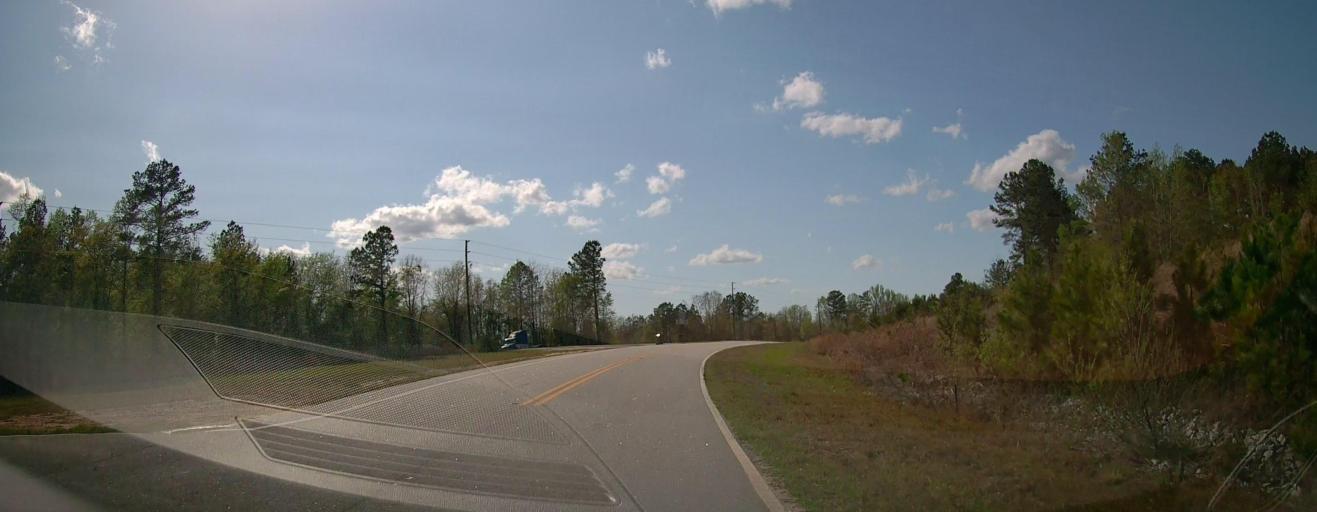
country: US
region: Georgia
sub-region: Baldwin County
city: Hardwick
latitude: 33.0174
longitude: -83.1053
